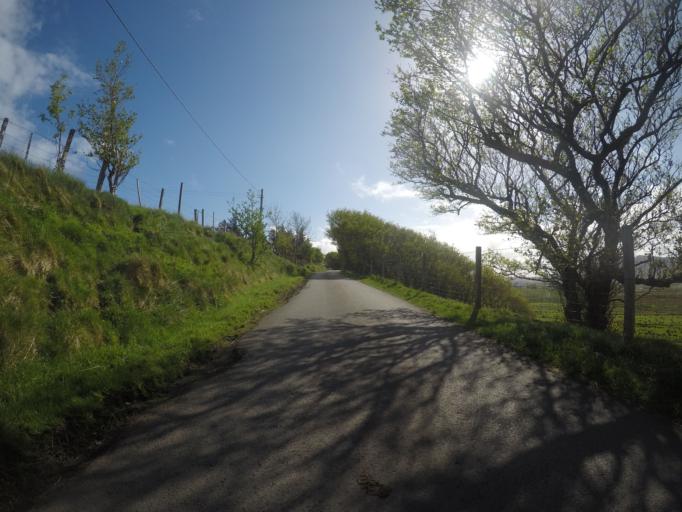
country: GB
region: Scotland
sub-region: Highland
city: Portree
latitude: 57.6326
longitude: -6.2174
